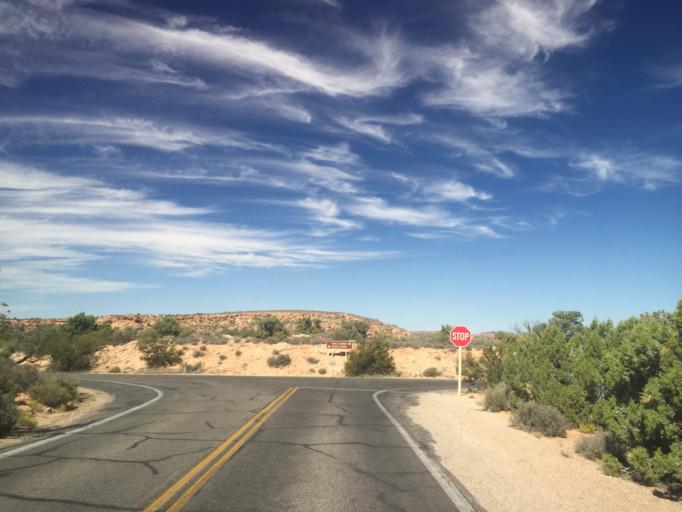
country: US
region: Utah
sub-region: Grand County
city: Moab
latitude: 38.7037
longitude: -109.5629
